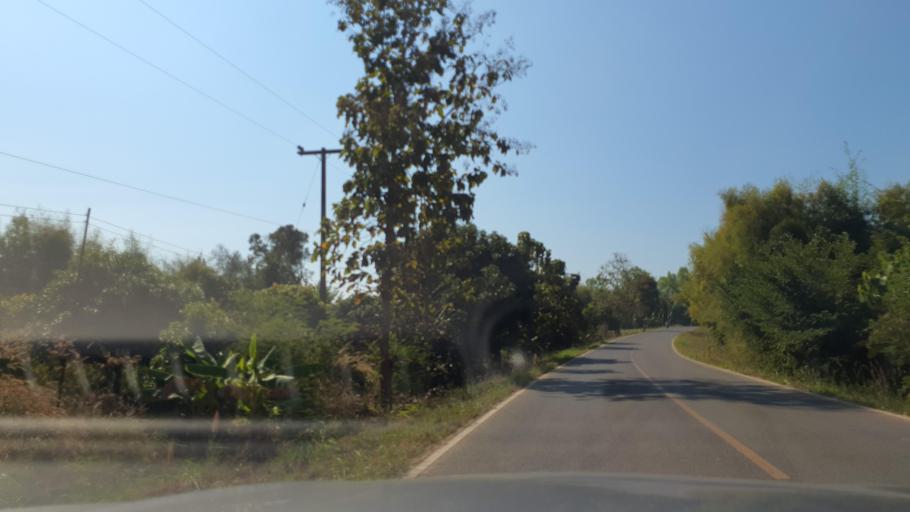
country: TH
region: Nan
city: Pua
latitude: 19.1243
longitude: 100.9211
